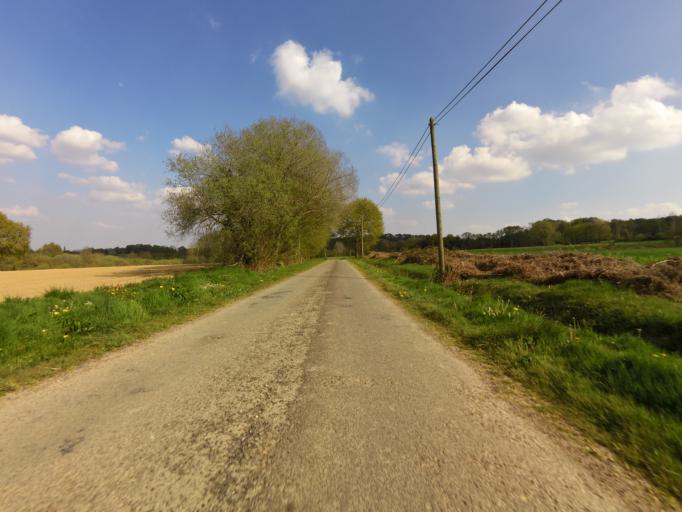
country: FR
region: Brittany
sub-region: Departement du Morbihan
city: Pluherlin
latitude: 47.7104
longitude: -2.3416
